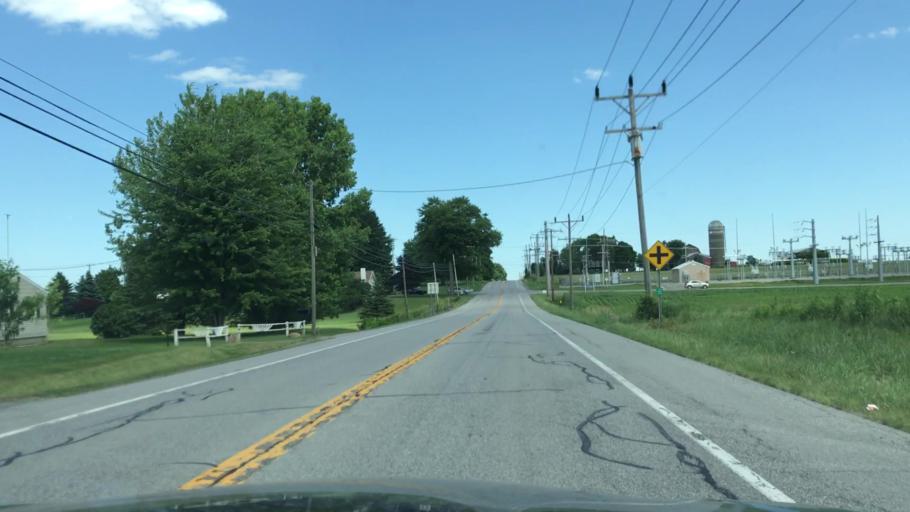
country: US
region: New York
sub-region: Wyoming County
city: Perry
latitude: 42.7470
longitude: -78.0275
